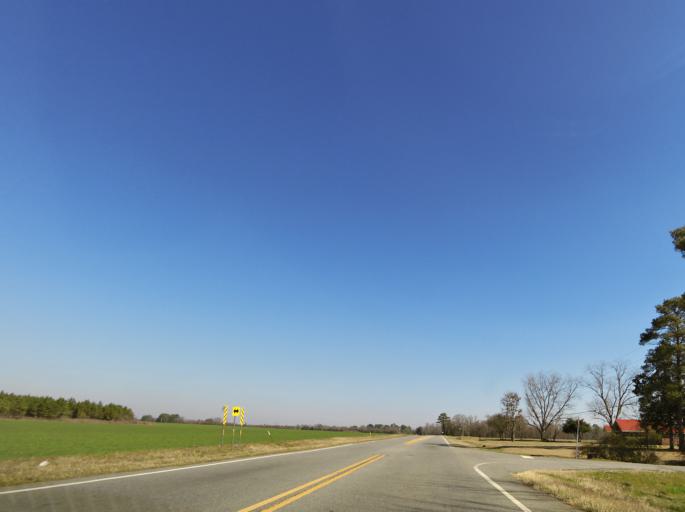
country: US
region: Georgia
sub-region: Bleckley County
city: Cochran
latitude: 32.3499
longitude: -83.3950
